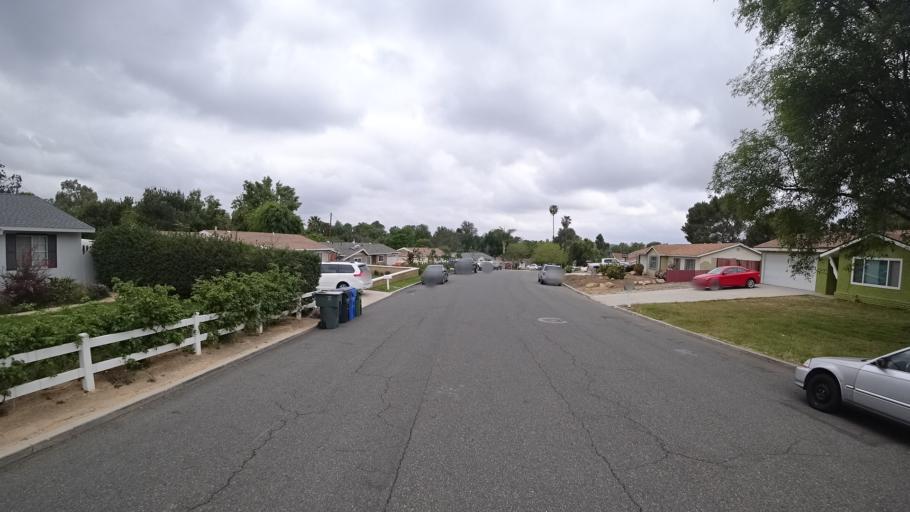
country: US
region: California
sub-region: Ventura County
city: Thousand Oaks
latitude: 34.2111
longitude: -118.8625
